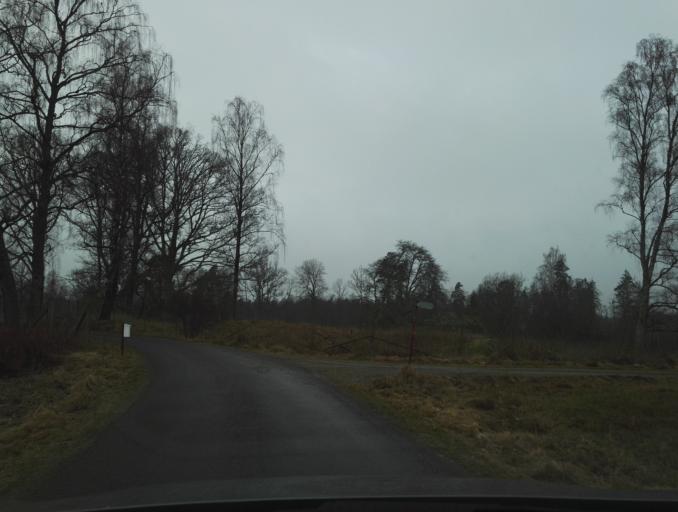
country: SE
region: Kronoberg
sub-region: Vaxjo Kommun
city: Vaexjoe
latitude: 56.9423
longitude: 14.7638
